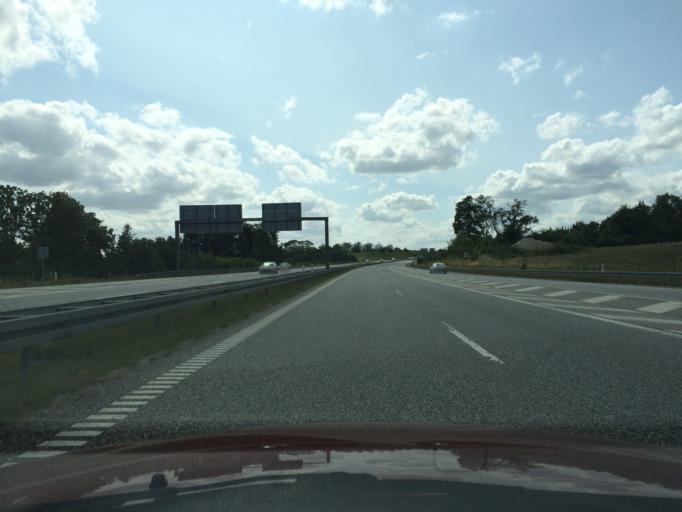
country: DK
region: Central Jutland
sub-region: Arhus Kommune
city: Framlev
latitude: 56.1549
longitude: 10.0373
